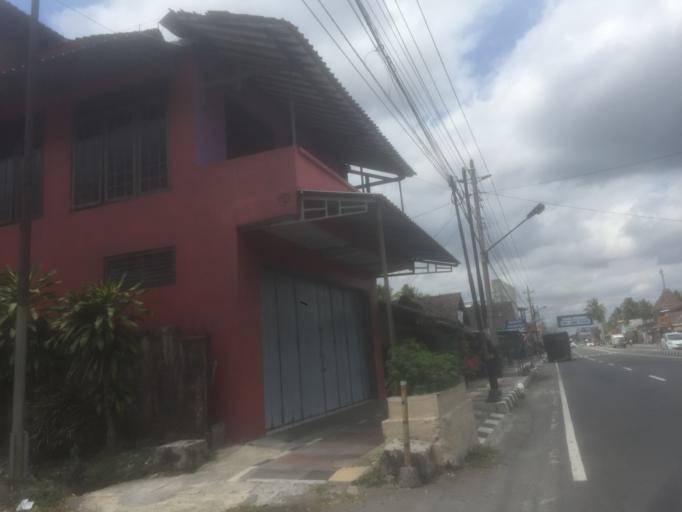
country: ID
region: Central Java
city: Muntilan
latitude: -7.6371
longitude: 110.3208
